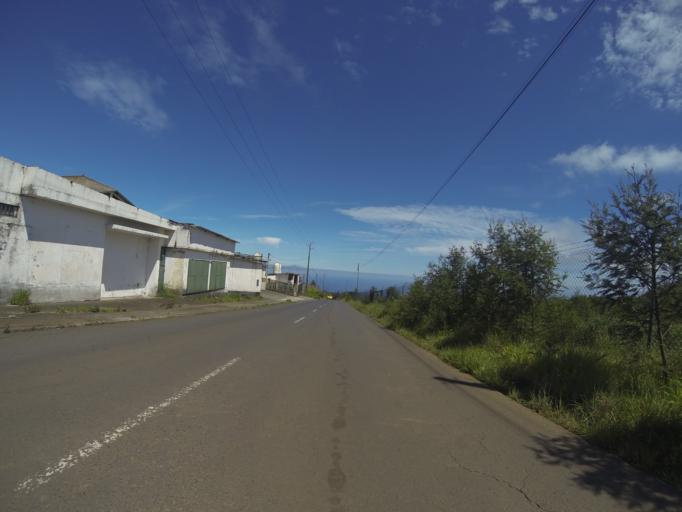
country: PT
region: Madeira
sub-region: Santa Cruz
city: Camacha
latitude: 32.7155
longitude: -16.8307
